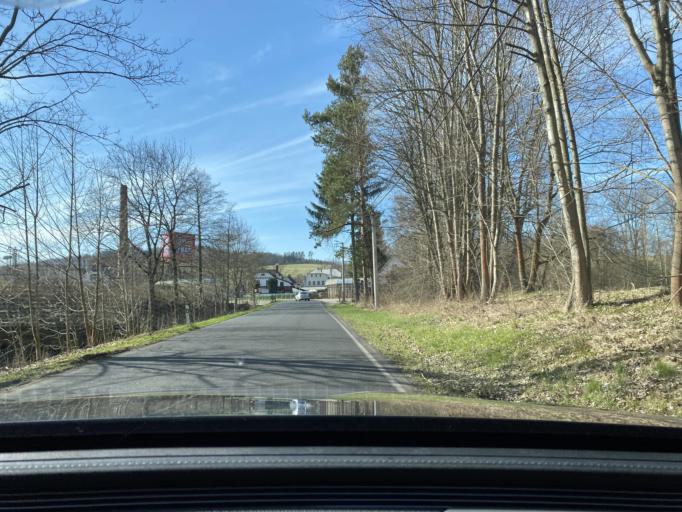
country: CZ
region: Ustecky
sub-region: Okres Decin
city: Sluknov
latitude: 51.0246
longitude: 14.4552
